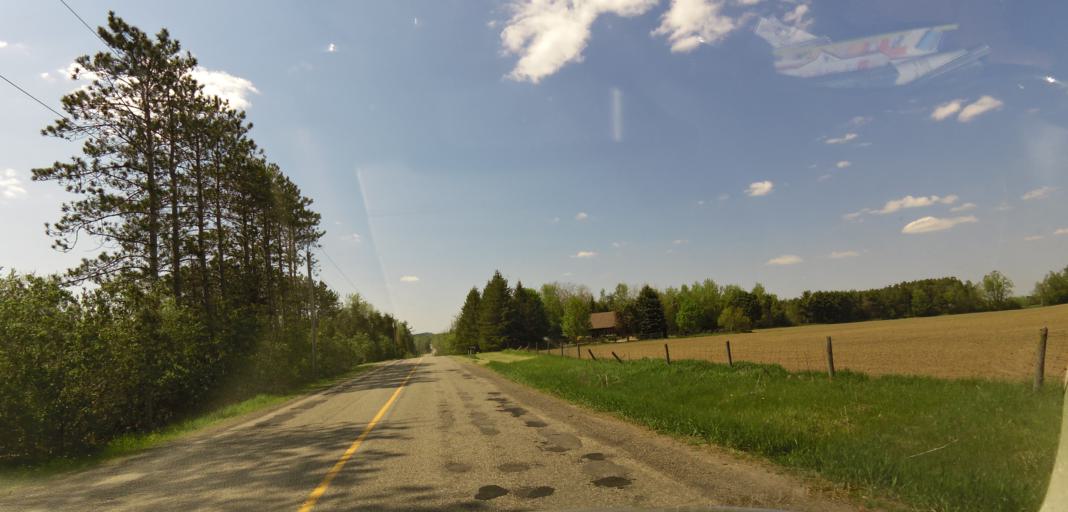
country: CA
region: Ontario
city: Brampton
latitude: 43.8444
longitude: -79.8787
